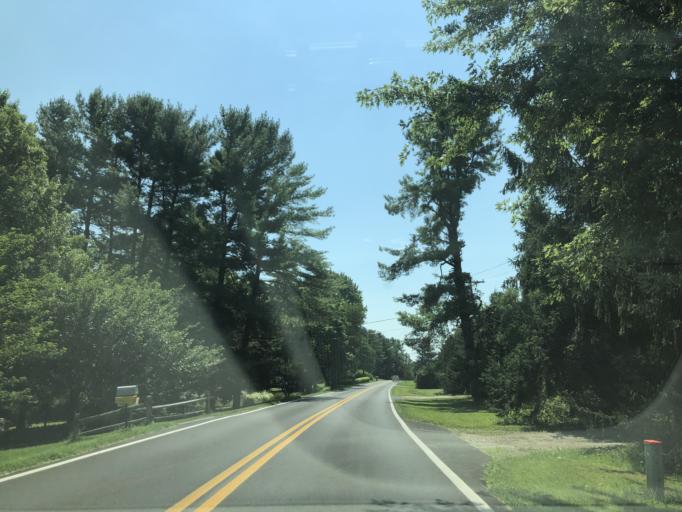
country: US
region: Maryland
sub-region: Carroll County
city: Eldersburg
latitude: 39.4436
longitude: -76.9588
